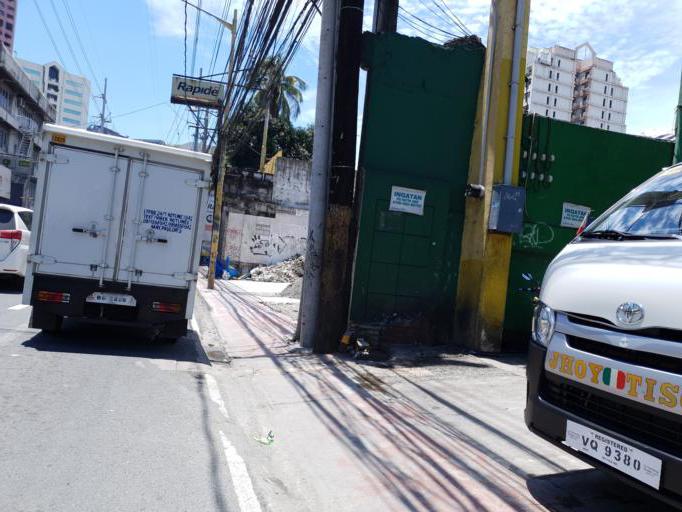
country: PH
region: Metro Manila
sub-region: Makati City
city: Makati City
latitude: 14.5644
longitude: 121.0117
